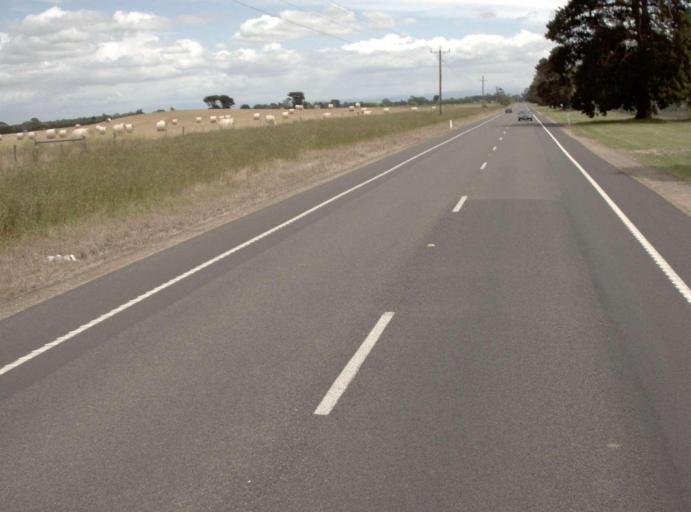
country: AU
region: Victoria
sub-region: Wellington
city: Sale
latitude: -38.0766
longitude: 147.0455
